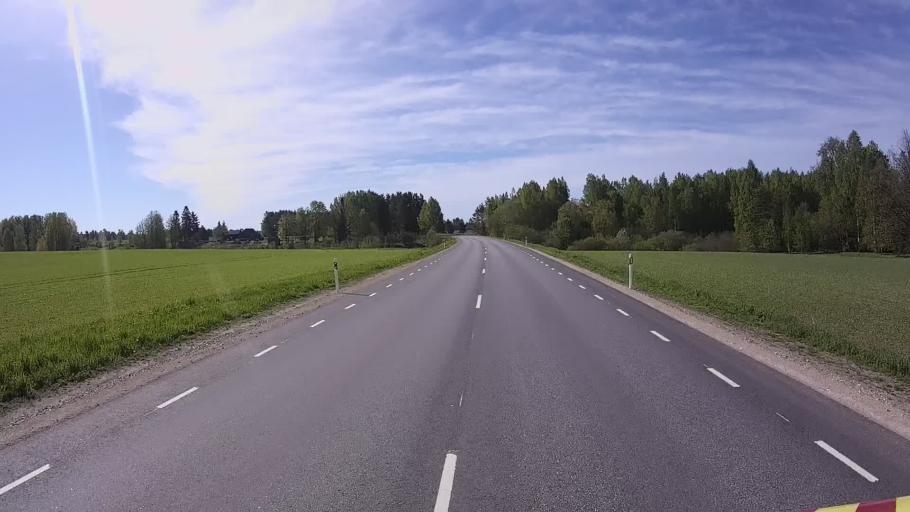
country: EE
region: Tartu
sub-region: UElenurme vald
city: Ulenurme
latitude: 58.3185
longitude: 26.9857
